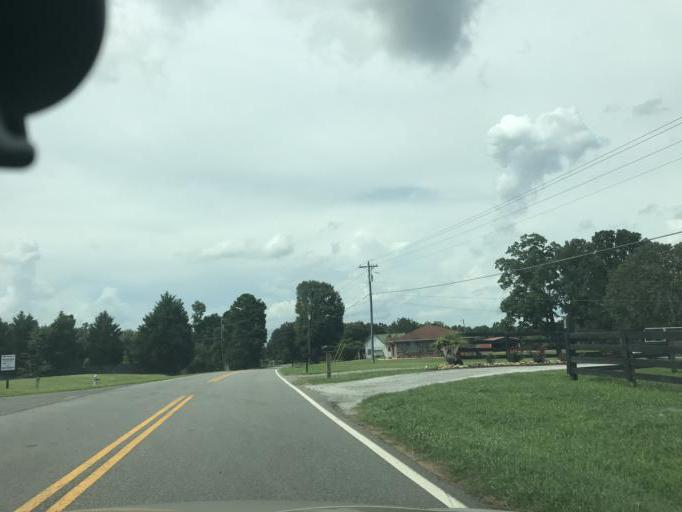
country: US
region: Georgia
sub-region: Forsyth County
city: Cumming
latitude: 34.2586
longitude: -84.2388
